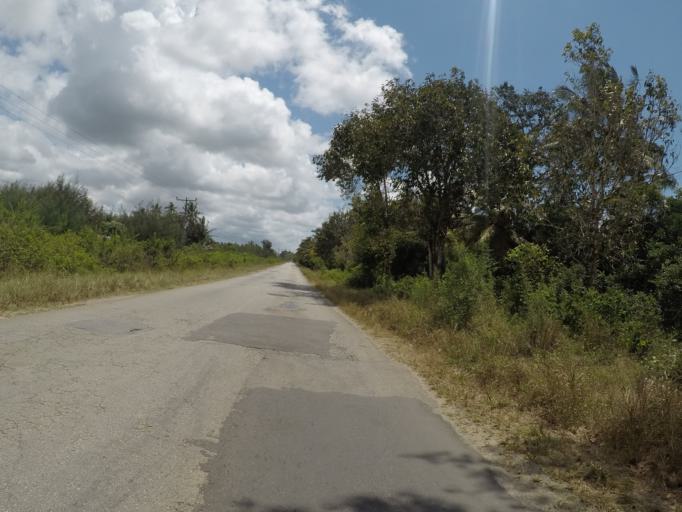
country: TZ
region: Zanzibar Central/South
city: Nganane
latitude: -6.2755
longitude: 39.4309
